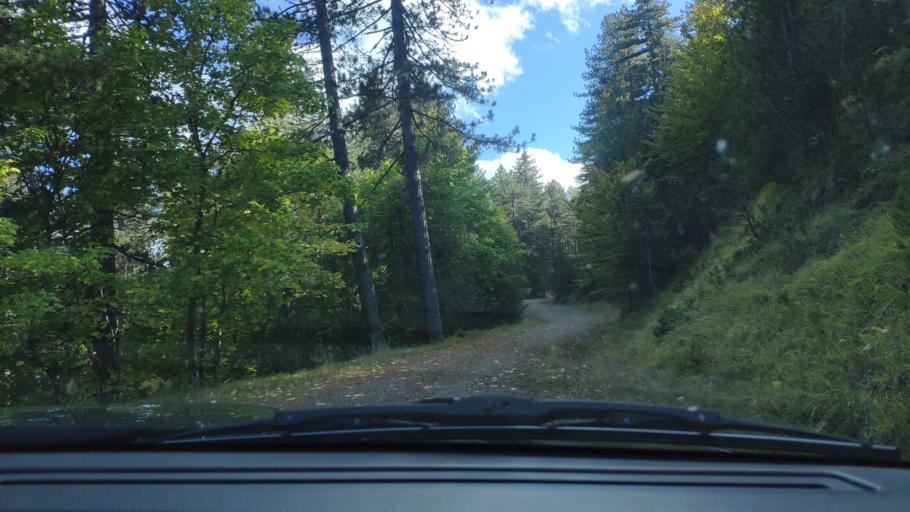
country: AL
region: Korce
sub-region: Rrethi i Devollit
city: Miras
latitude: 40.3844
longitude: 20.8862
